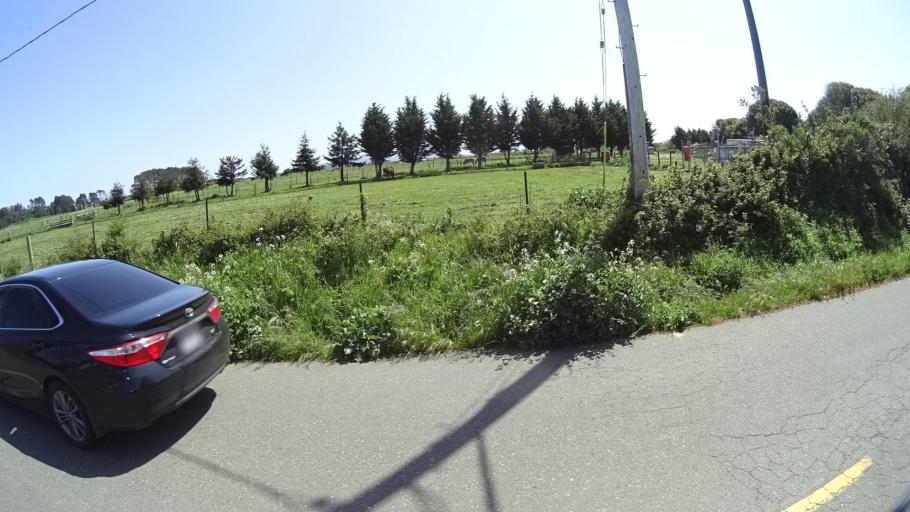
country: US
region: California
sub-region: Humboldt County
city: Fortuna
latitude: 40.5630
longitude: -124.1384
